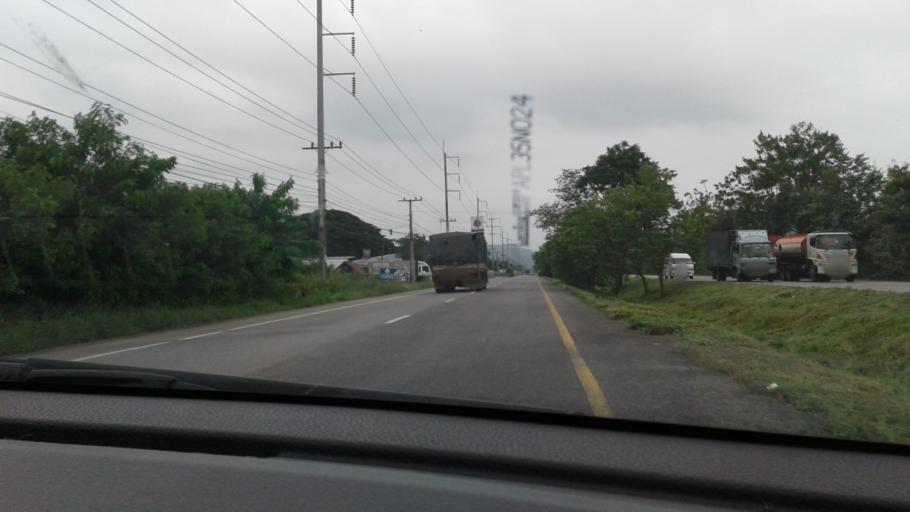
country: TH
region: Prachuap Khiri Khan
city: Prachuap Khiri Khan
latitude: 11.8592
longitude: 99.7841
